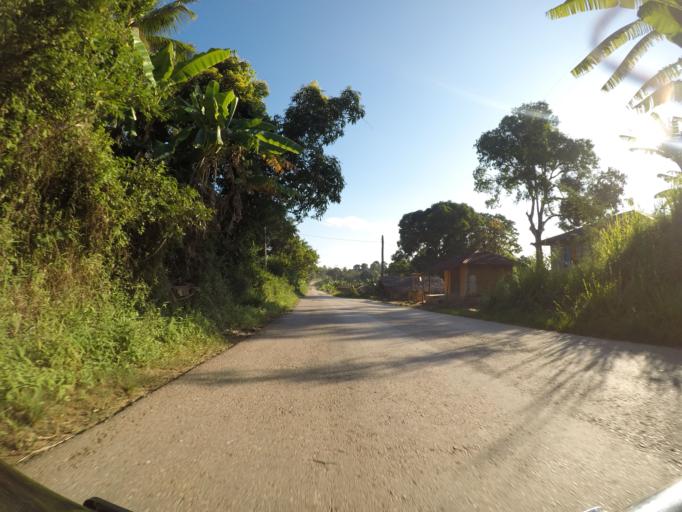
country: TZ
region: Pemba South
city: Mtambile
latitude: -5.3376
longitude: 39.7305
